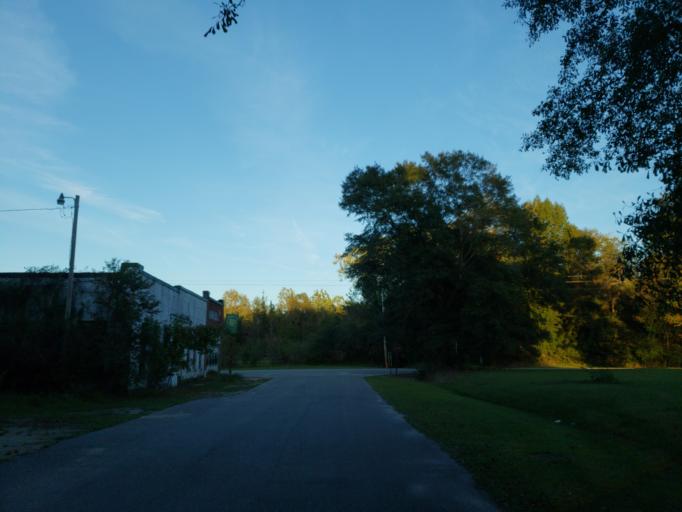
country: US
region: Mississippi
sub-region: Wayne County
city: Belmont
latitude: 31.4340
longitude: -88.4775
